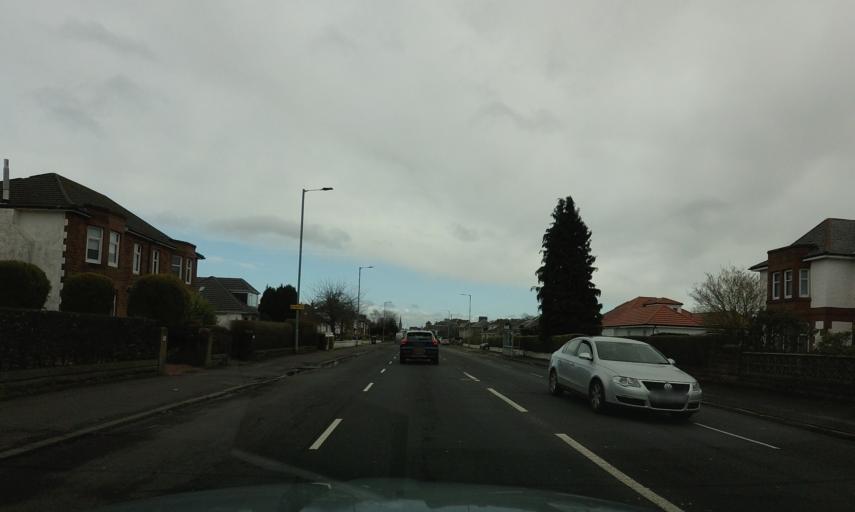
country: GB
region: Scotland
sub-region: East Renfrewshire
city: Giffnock
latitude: 55.8344
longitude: -4.2914
